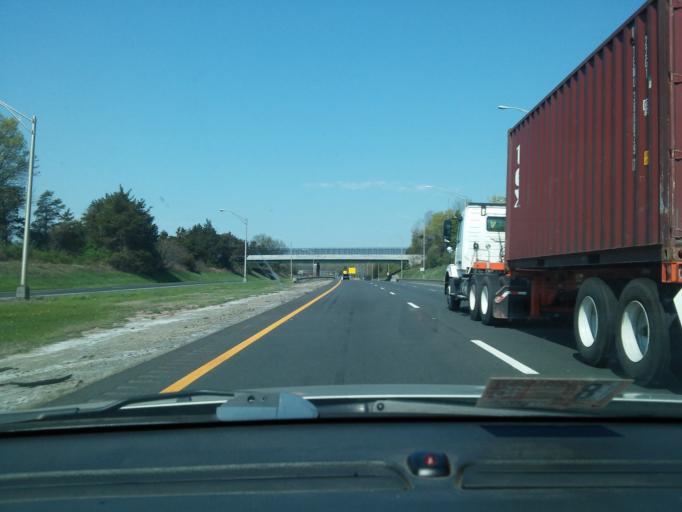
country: US
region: New Jersey
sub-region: Somerset County
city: Bedminster
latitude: 40.6436
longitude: -74.6528
